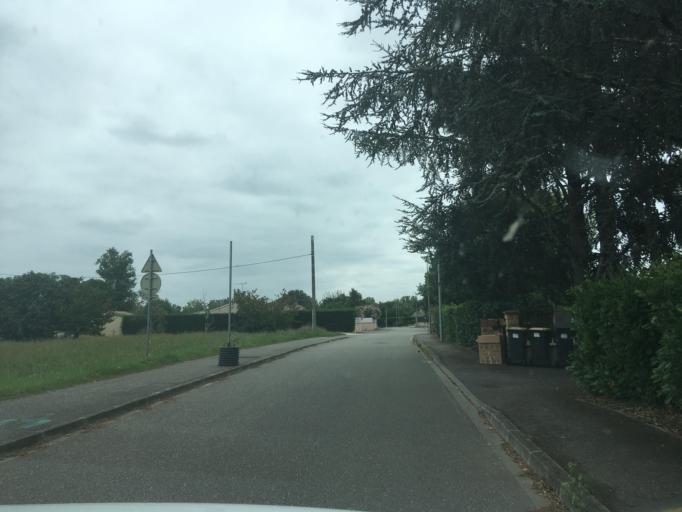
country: FR
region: Aquitaine
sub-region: Departement du Lot-et-Garonne
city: Roquefort
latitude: 44.1730
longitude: 0.5728
